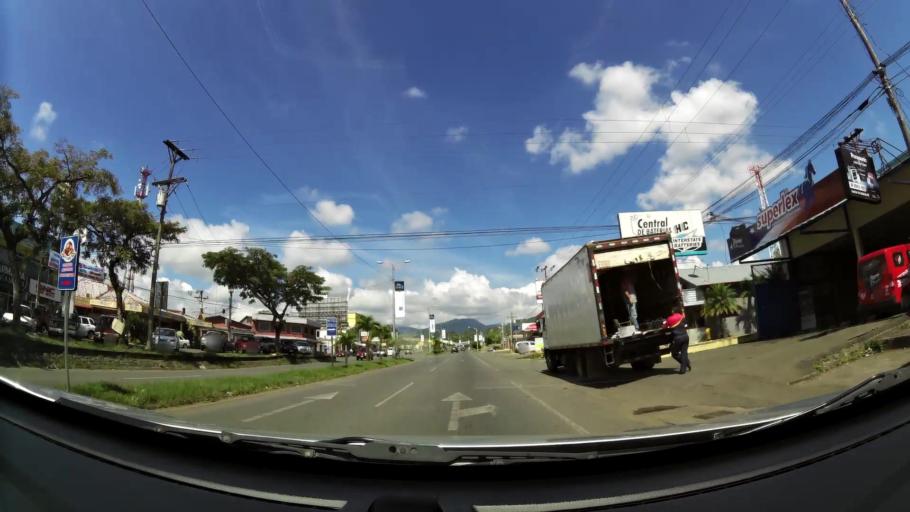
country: CR
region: San Jose
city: San Isidro
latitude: 9.3772
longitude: -83.7036
